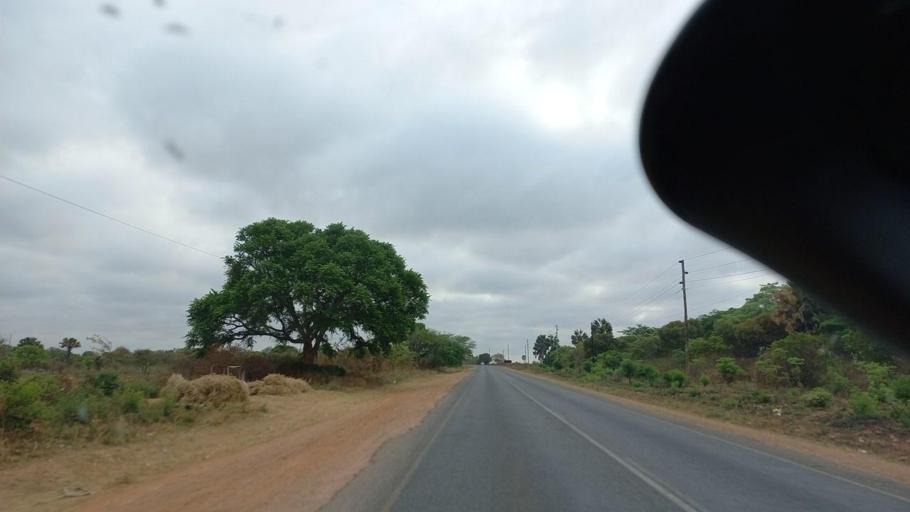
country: ZM
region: Lusaka
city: Chongwe
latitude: -15.3474
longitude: 28.5782
